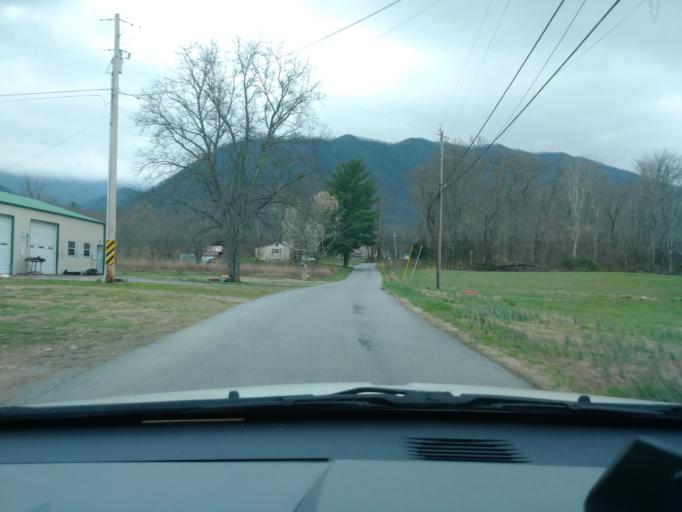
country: US
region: Tennessee
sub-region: Greene County
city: Tusculum
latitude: 36.0772
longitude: -82.7244
